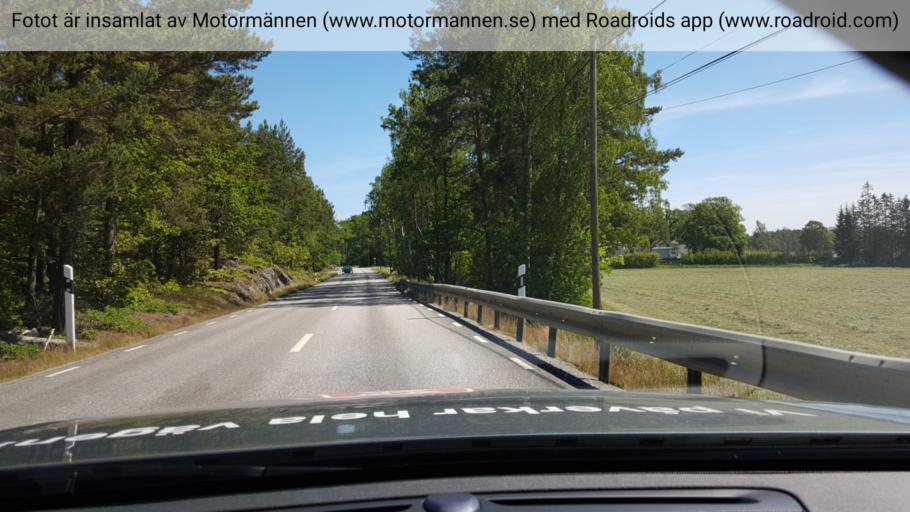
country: SE
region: Stockholm
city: Dalaro
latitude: 59.1255
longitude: 18.3193
